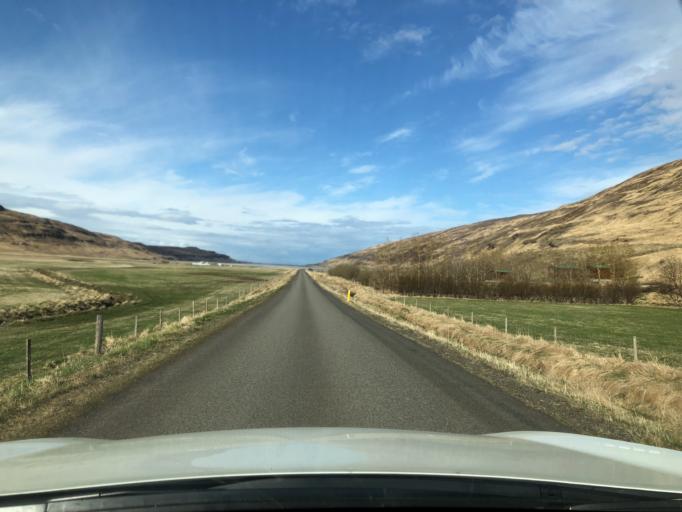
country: IS
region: West
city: Borgarnes
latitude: 65.0579
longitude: -21.5495
